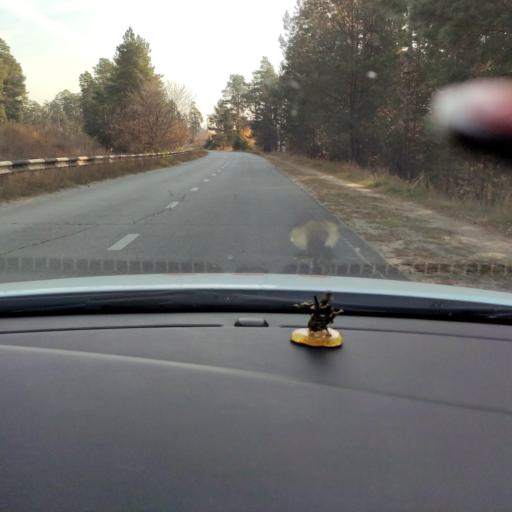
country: RU
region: Tatarstan
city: Staroye Arakchino
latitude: 55.8243
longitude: 48.9112
